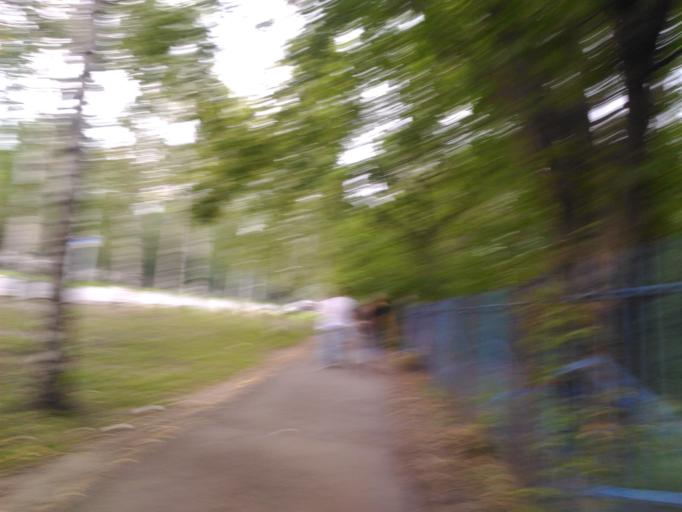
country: RU
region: Ulyanovsk
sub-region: Ulyanovskiy Rayon
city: Ulyanovsk
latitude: 54.2685
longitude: 48.3350
